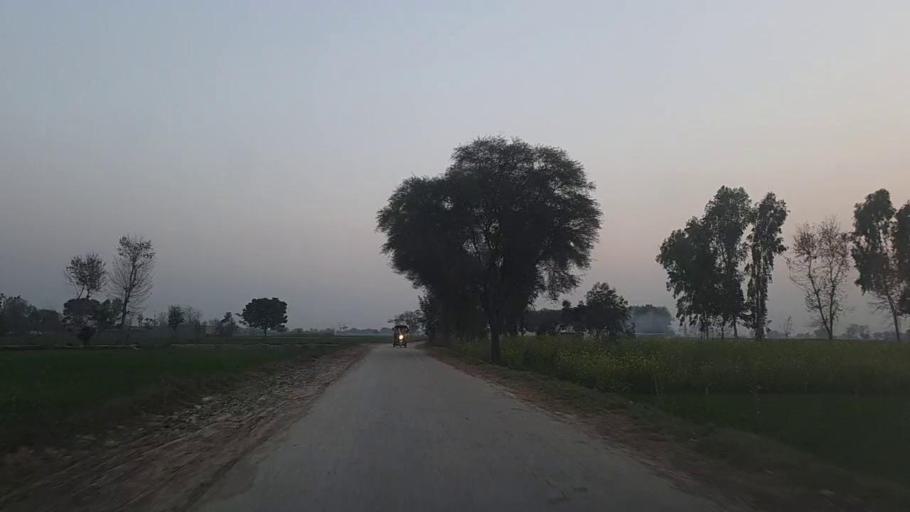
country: PK
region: Sindh
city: Naushahro Firoz
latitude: 26.8650
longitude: 68.0475
